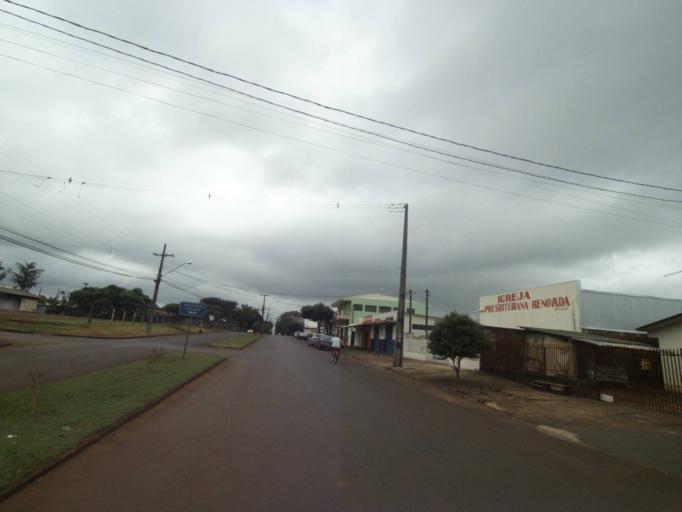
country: BR
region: Parana
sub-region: Campo Mourao
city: Campo Mourao
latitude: -24.0194
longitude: -52.3556
